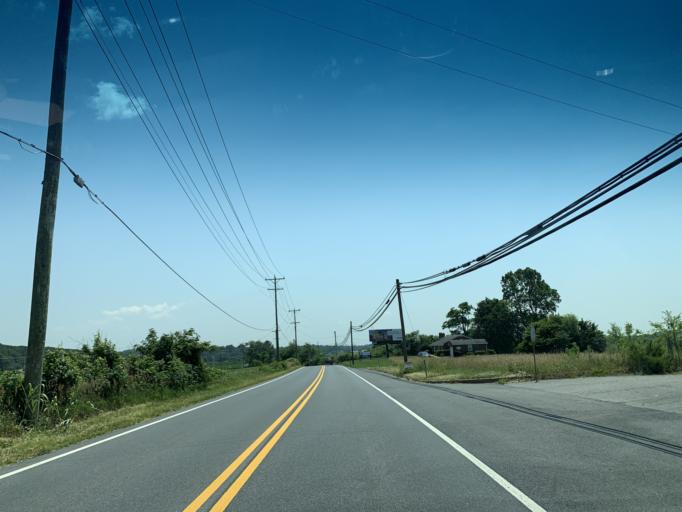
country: US
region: Maryland
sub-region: Frederick County
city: Green Valley
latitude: 39.3498
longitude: -77.2707
